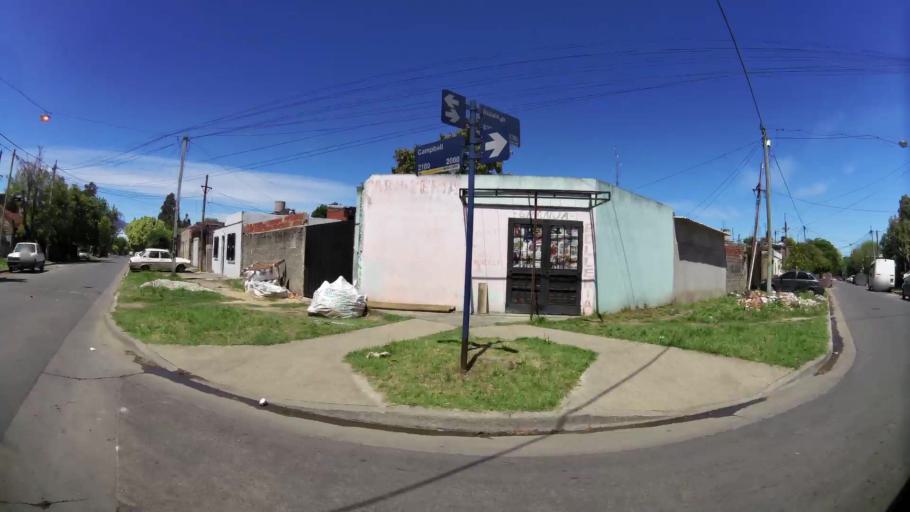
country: AR
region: Santa Fe
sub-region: Departamento de Rosario
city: Rosario
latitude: -32.9521
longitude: -60.7075
